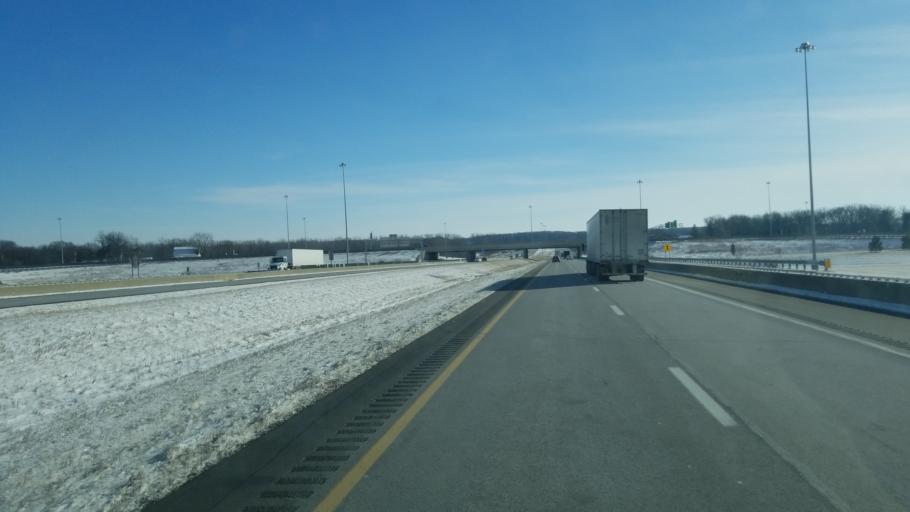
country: US
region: Ohio
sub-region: Lucas County
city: Maumee
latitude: 41.5564
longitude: -83.6871
